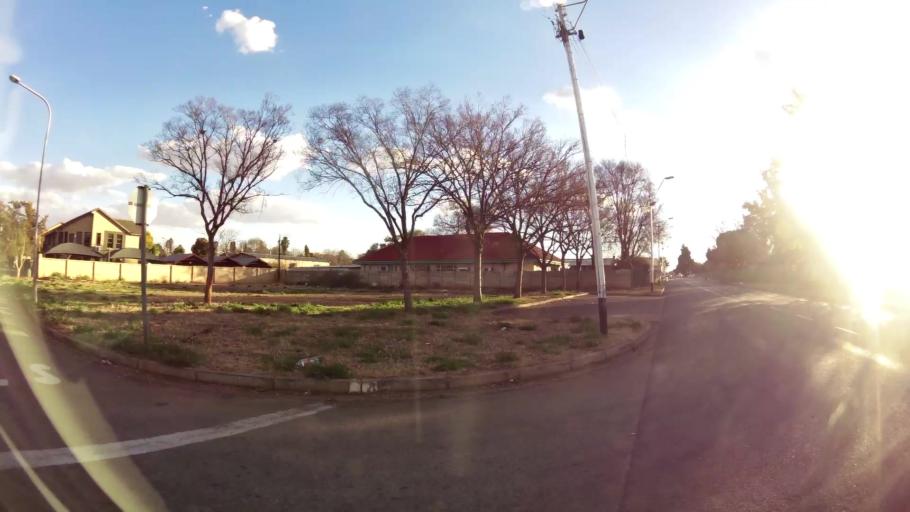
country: ZA
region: North-West
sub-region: Dr Kenneth Kaunda District Municipality
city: Potchefstroom
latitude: -26.7166
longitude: 27.1009
